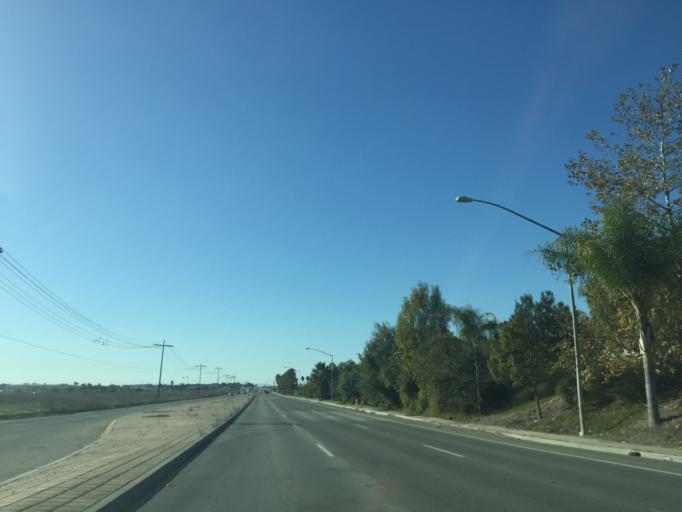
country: MX
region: Baja California
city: Tijuana
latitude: 32.5677
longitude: -116.9555
